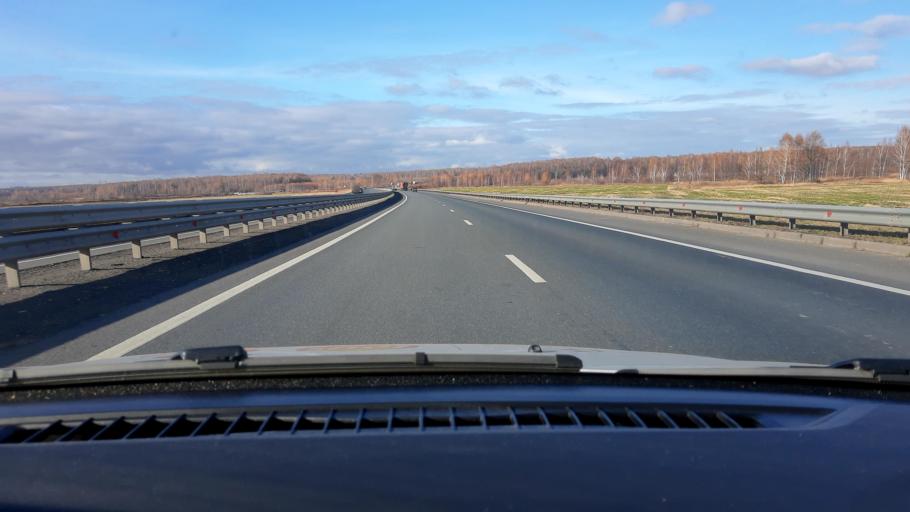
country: RU
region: Nizjnij Novgorod
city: Burevestnik
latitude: 56.1235
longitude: 43.8024
